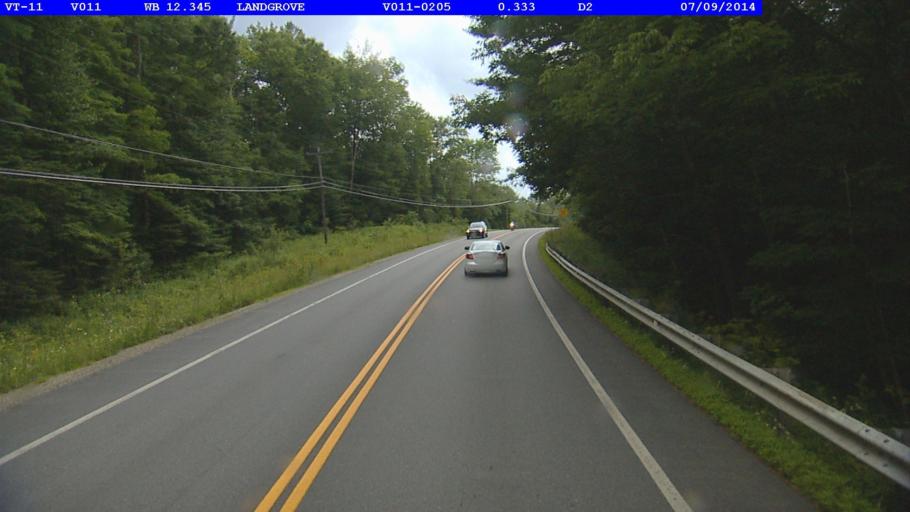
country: US
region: Vermont
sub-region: Bennington County
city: Manchester Center
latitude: 43.2359
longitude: -72.8590
